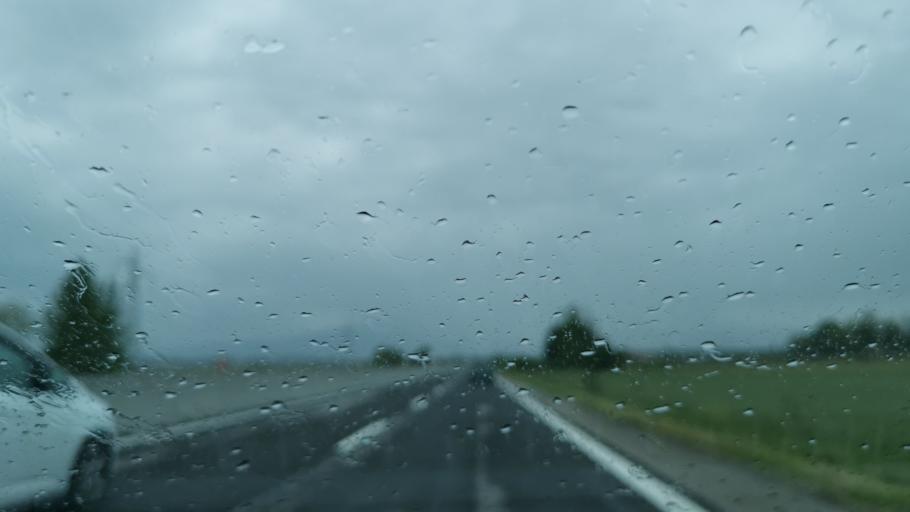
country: IT
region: Veneto
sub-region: Provincia di Verona
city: Castelnuovo del Garda
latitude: 45.4493
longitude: 10.7484
